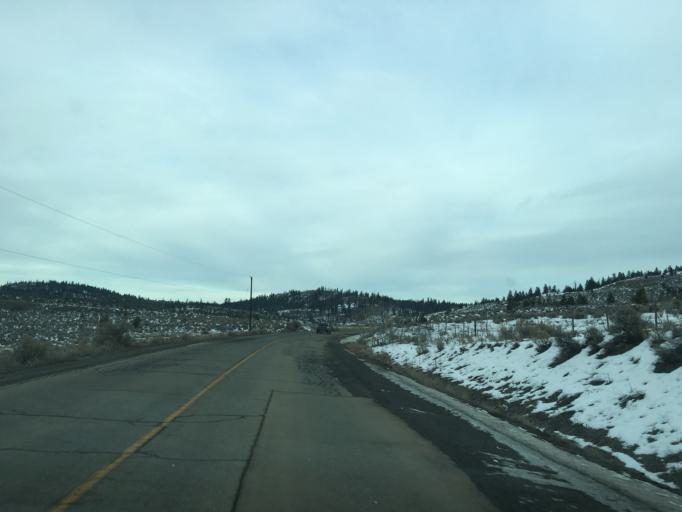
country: CA
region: British Columbia
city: Kamloops
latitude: 50.6259
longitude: -120.4428
